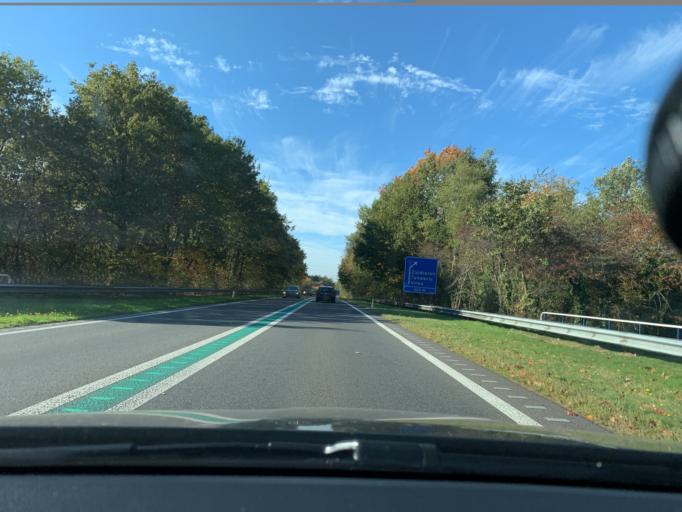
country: NL
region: Drenthe
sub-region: Gemeente Tynaarlo
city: Zuidlaren
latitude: 53.0798
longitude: 6.6710
